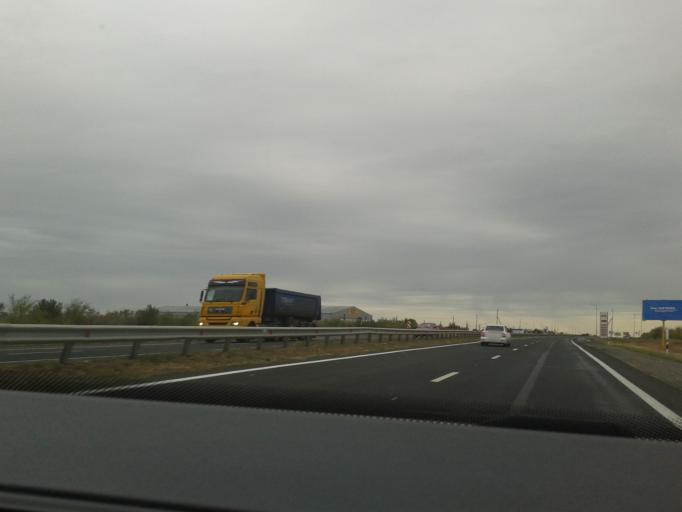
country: RU
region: Volgograd
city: Gorodishche
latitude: 48.8303
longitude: 44.4233
